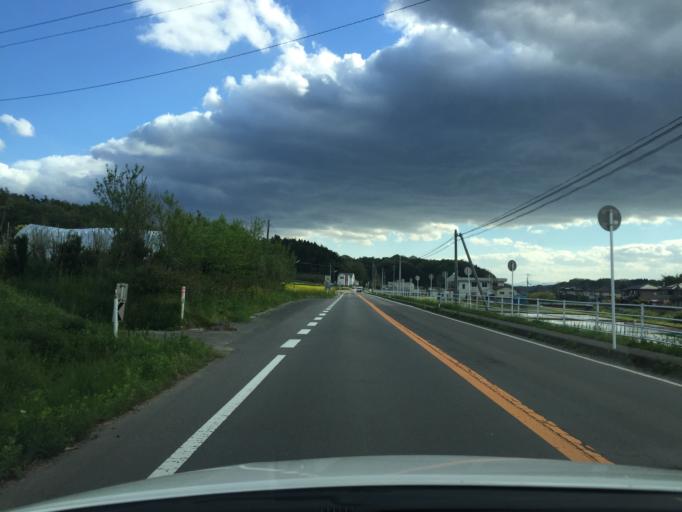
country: JP
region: Fukushima
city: Fukushima-shi
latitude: 37.6689
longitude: 140.5563
